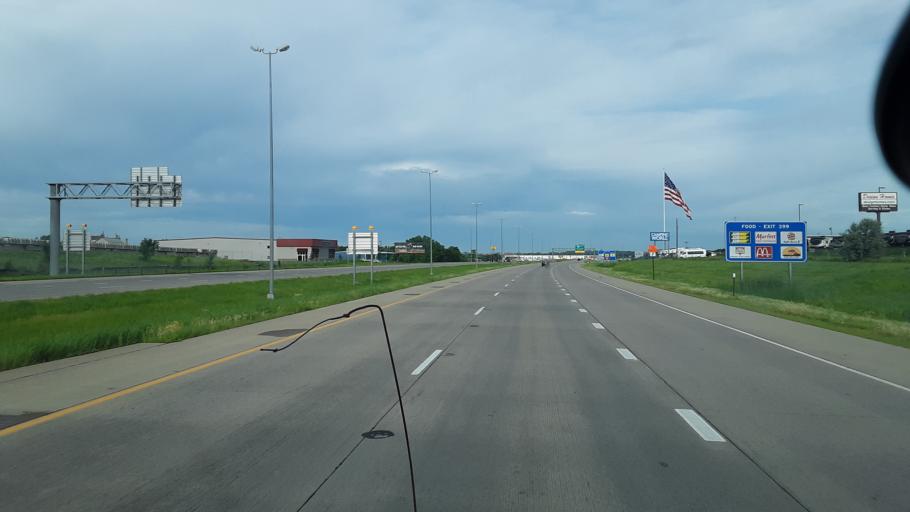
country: US
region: South Dakota
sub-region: Minnehaha County
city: Sioux Falls
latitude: 43.6061
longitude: -96.7005
